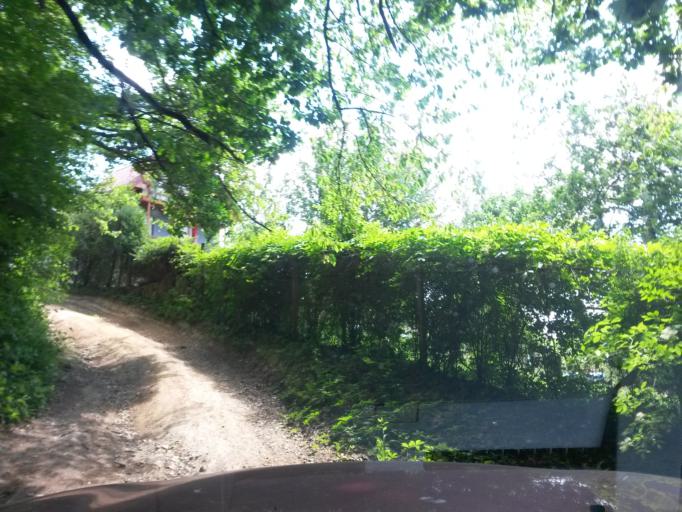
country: SK
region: Kosicky
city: Kosice
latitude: 48.7381
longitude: 21.1198
